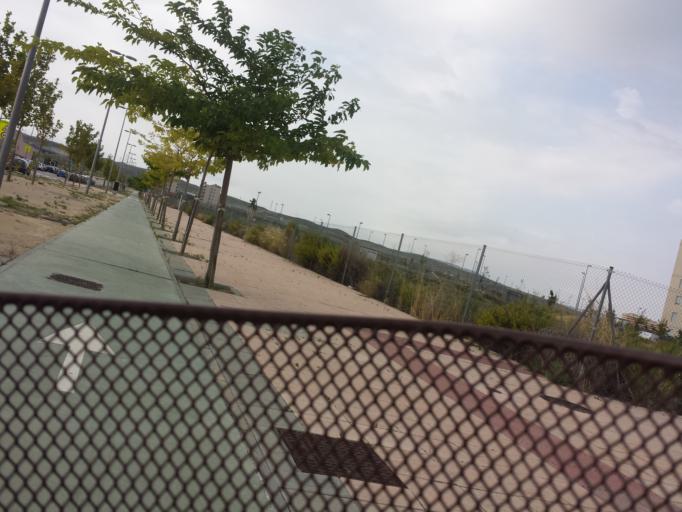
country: ES
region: Aragon
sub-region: Provincia de Zaragoza
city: Montecanal
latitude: 41.6264
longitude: -0.9572
